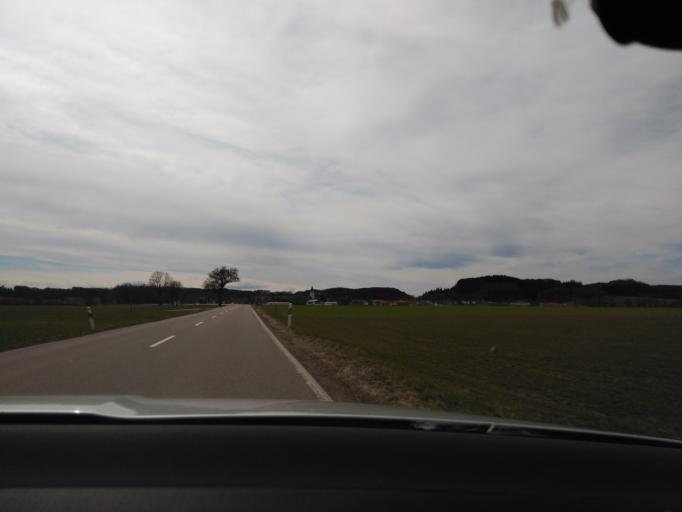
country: DE
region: Baden-Wuerttemberg
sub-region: Tuebingen Region
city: Aichstetten
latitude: 47.9039
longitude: 10.0899
